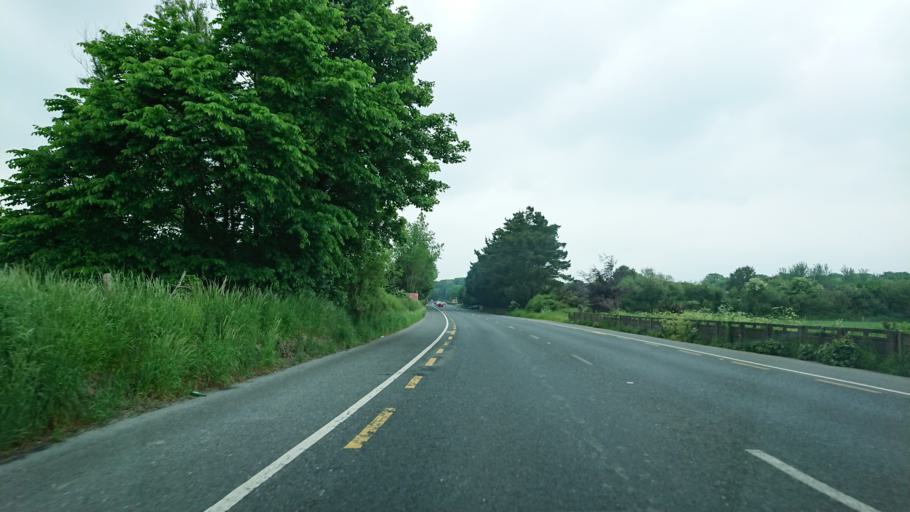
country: IE
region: Munster
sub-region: Waterford
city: Waterford
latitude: 52.2037
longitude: -7.1163
